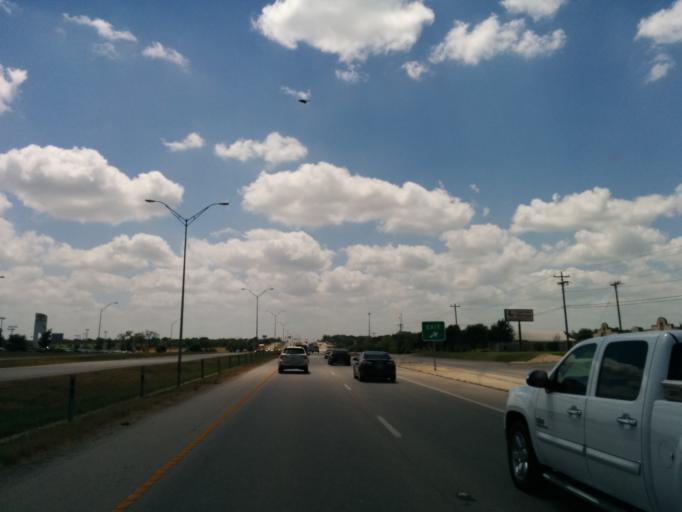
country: US
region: Texas
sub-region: Bastrop County
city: Bastrop
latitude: 30.1113
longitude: -97.3559
